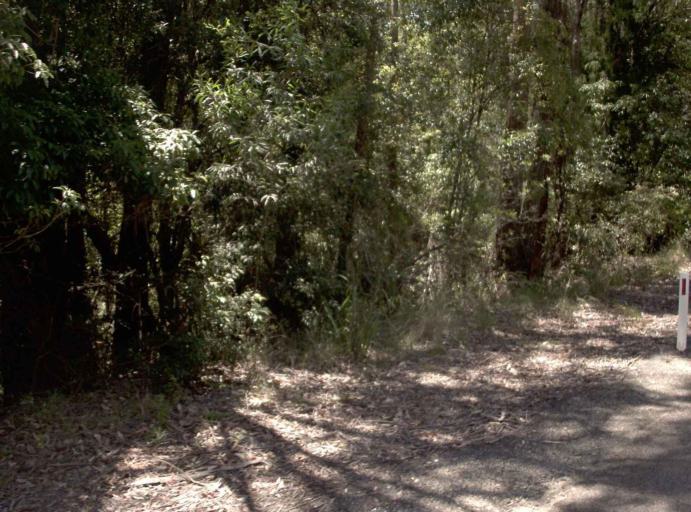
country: AU
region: Victoria
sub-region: East Gippsland
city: Lakes Entrance
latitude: -37.7063
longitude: 148.5752
